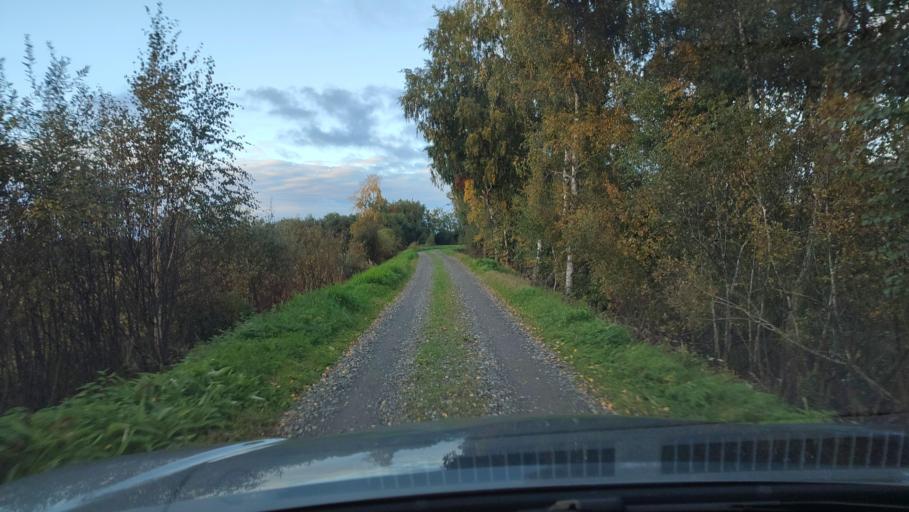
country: FI
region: Ostrobothnia
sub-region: Sydosterbotten
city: Kristinestad
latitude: 62.2332
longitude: 21.4509
